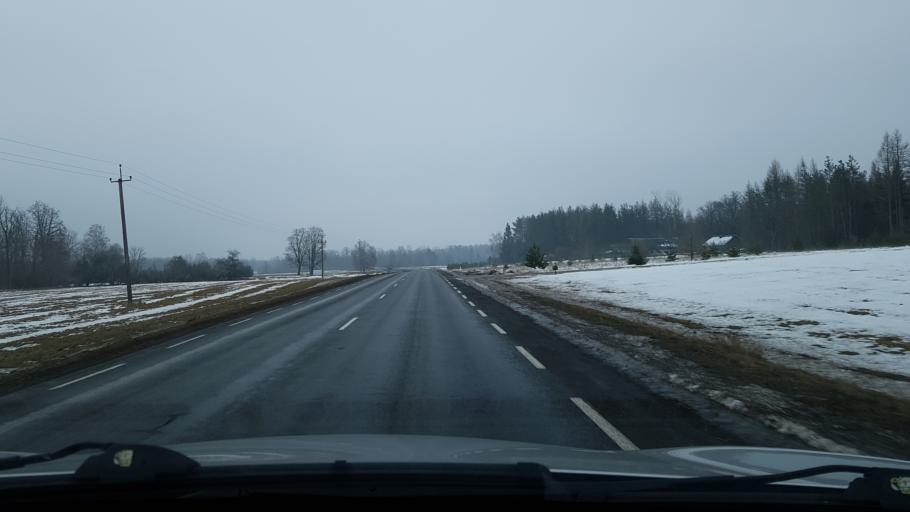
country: EE
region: Viljandimaa
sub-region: Viiratsi vald
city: Viiratsi
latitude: 58.2488
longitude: 25.7723
